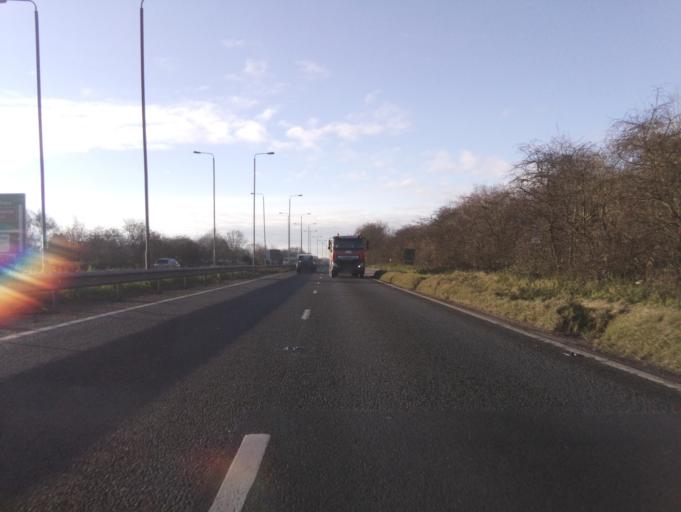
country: GB
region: England
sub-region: Derbyshire
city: Etwall
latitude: 52.8570
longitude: -1.5799
